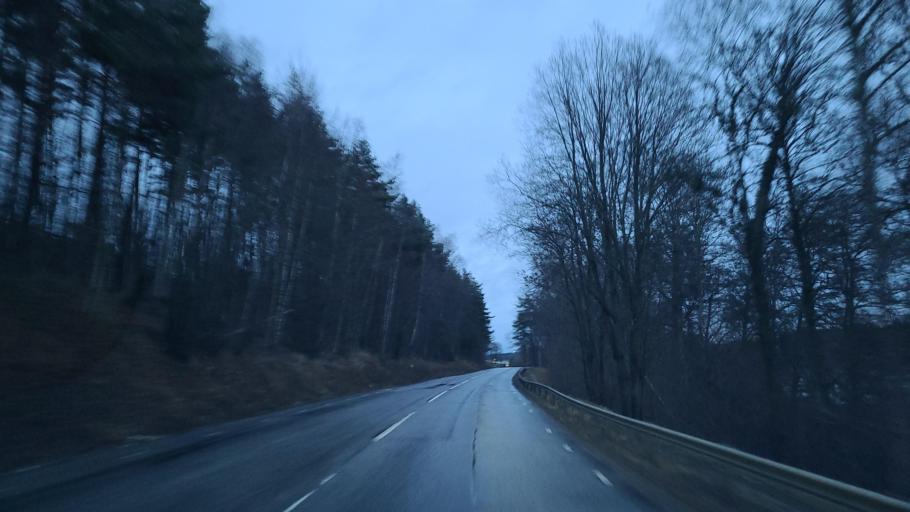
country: SE
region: Stockholm
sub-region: Norrtalje Kommun
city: Norrtalje
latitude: 59.7415
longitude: 18.6664
